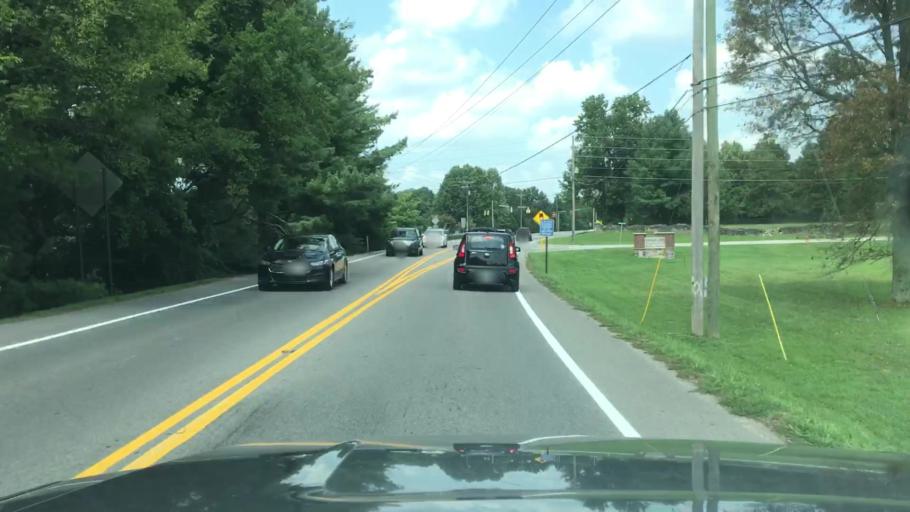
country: US
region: Tennessee
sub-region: Davidson County
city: Forest Hills
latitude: 36.0100
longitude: -86.8883
